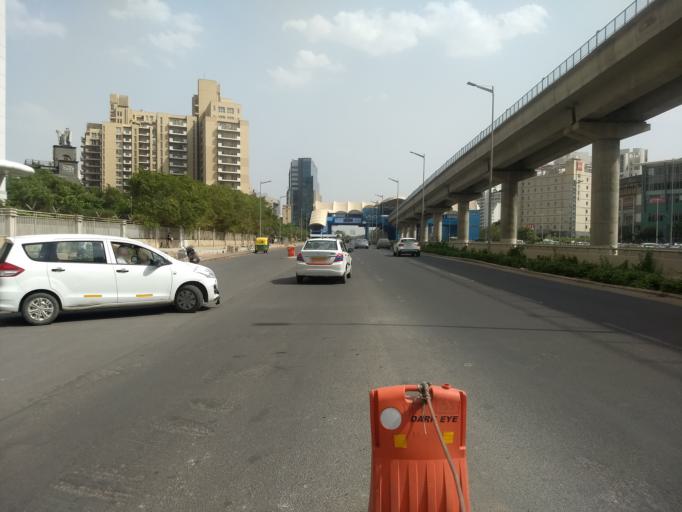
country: IN
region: Haryana
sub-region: Gurgaon
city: Gurgaon
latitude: 28.4489
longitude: 77.0999
